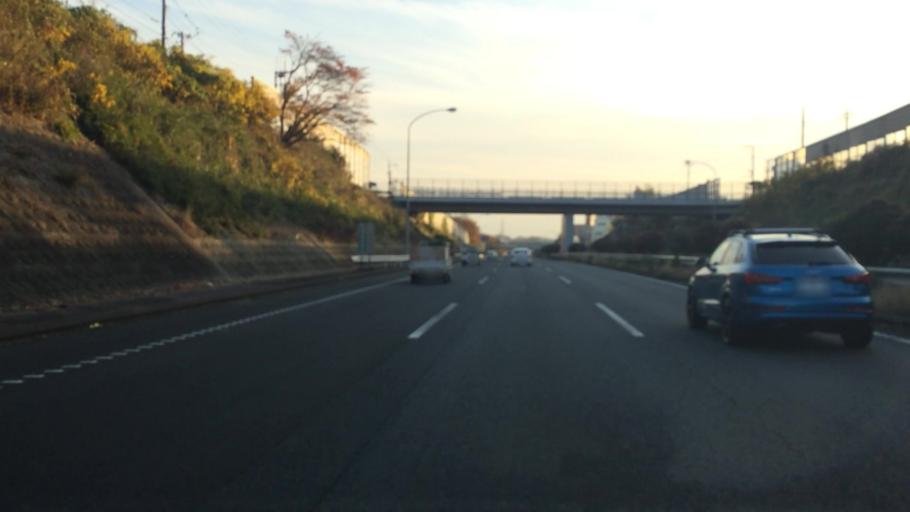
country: JP
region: Tokyo
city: Chofugaoka
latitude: 35.5797
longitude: 139.6176
